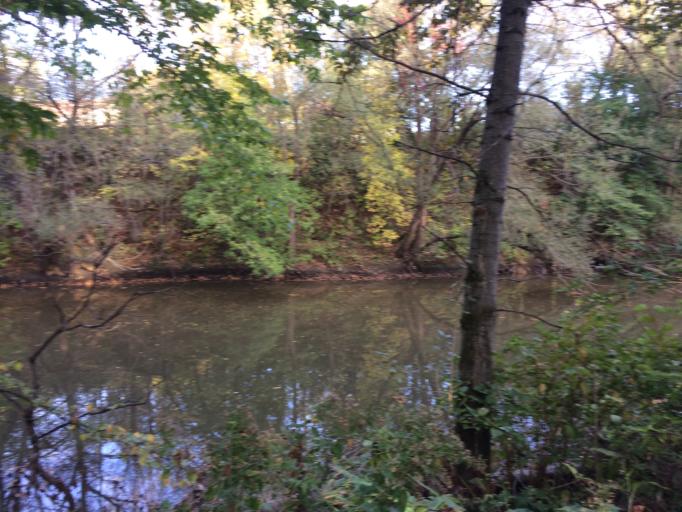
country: CA
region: Quebec
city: Quebec
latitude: 46.8110
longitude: -71.2701
